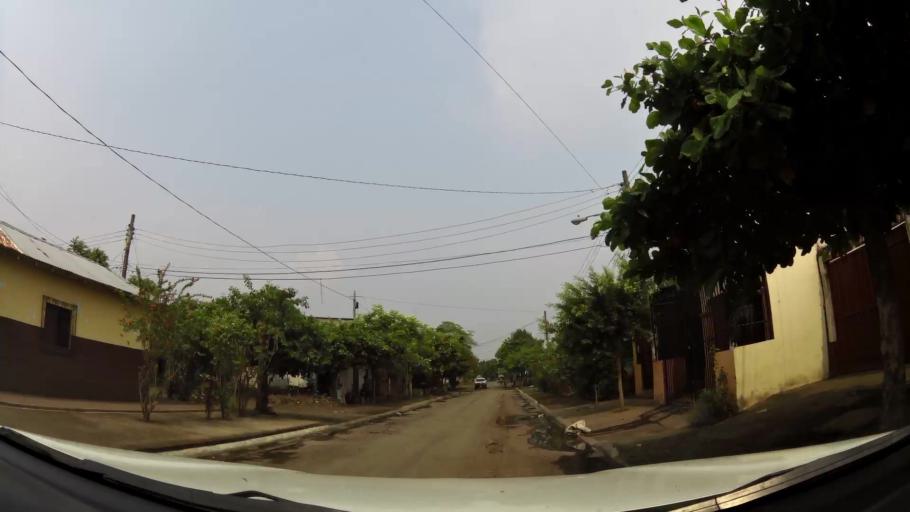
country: NI
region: Chinandega
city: Chinandega
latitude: 12.6304
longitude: -87.1440
